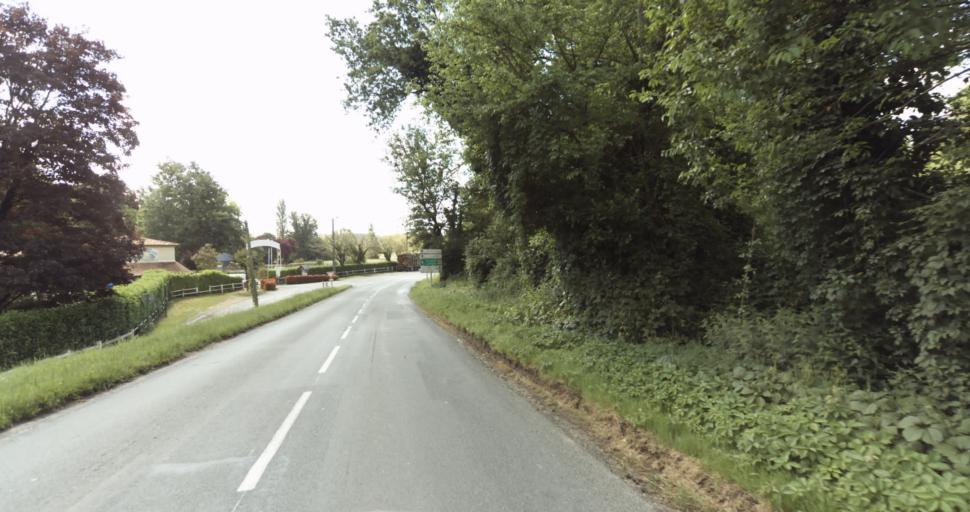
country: FR
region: Aquitaine
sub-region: Departement de la Dordogne
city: Le Bugue
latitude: 44.8540
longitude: 0.9097
